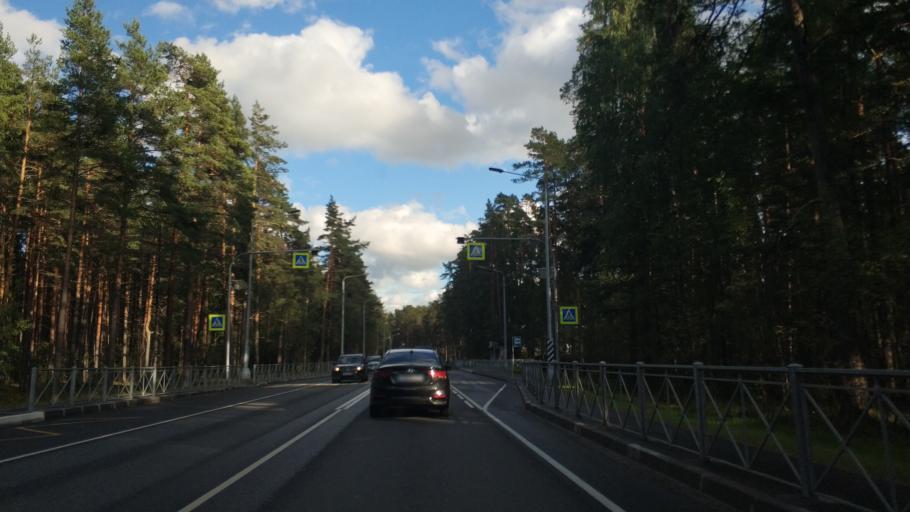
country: RU
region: Leningrad
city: Priozersk
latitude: 61.0109
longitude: 30.1598
